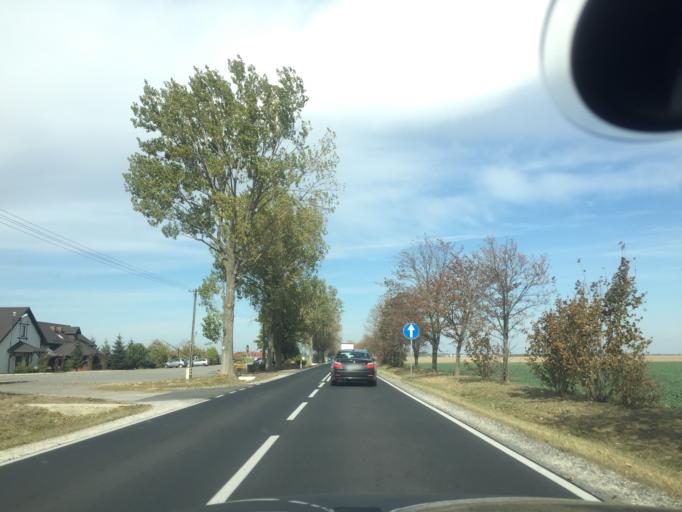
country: PL
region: Greater Poland Voivodeship
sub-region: Powiat gnieznienski
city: Czerniejewo
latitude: 52.4326
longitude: 17.5856
